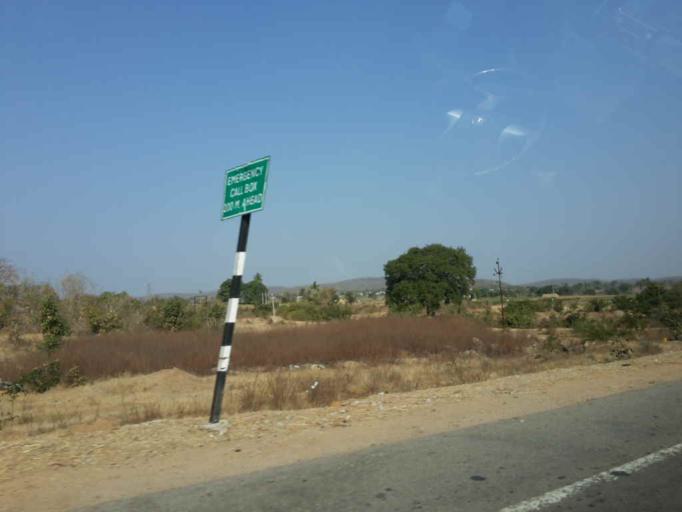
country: IN
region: Telangana
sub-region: Nizamabad District
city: Nizamabad
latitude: 18.5281
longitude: 78.2335
